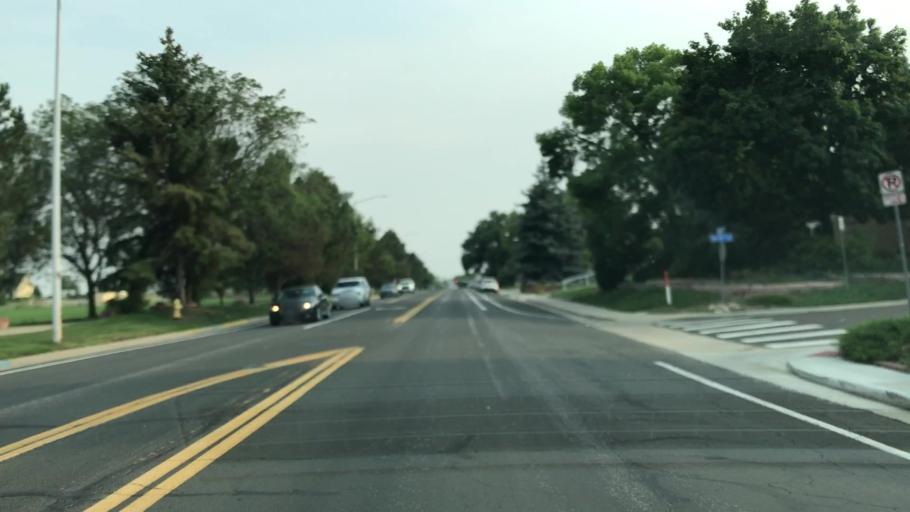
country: US
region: Colorado
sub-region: Broomfield County
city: Broomfield
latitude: 39.9279
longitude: -105.0718
